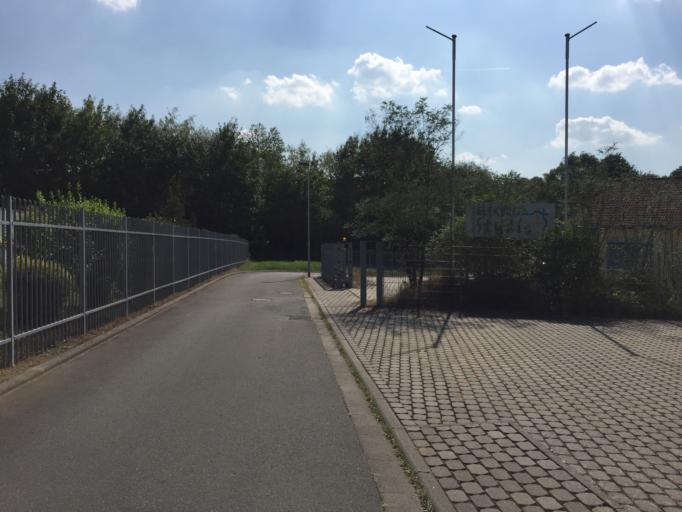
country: DE
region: Hesse
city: Solms
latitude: 50.5416
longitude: 8.4148
